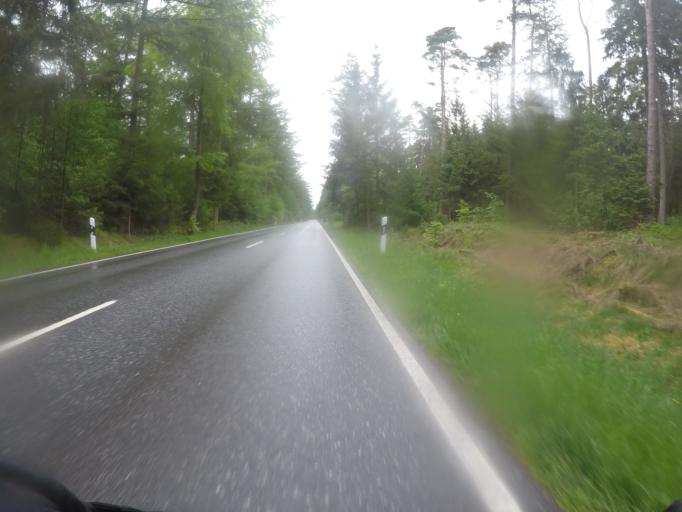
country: DE
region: Schleswig-Holstein
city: Heidmuhlen
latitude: 53.9400
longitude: 10.0880
